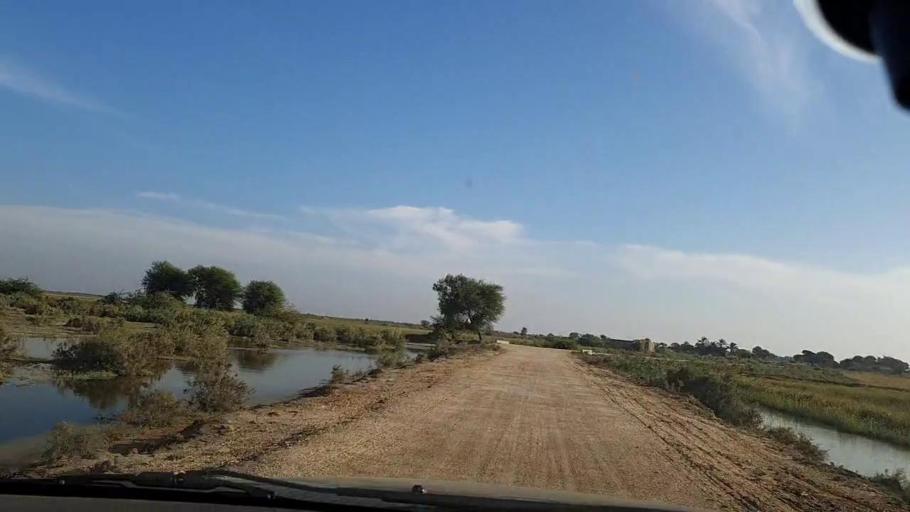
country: PK
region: Sindh
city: Mirpur Batoro
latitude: 24.6563
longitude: 68.3088
